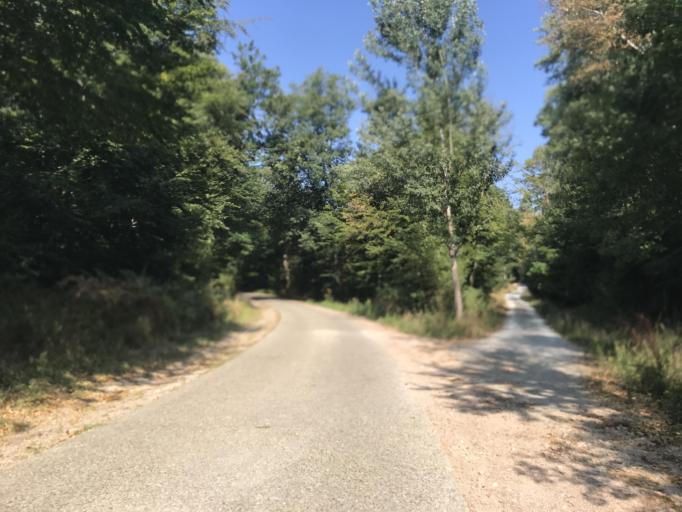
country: DE
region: Rheinland-Pfalz
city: Oestrich-Winkel
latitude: 50.0413
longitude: 8.0235
